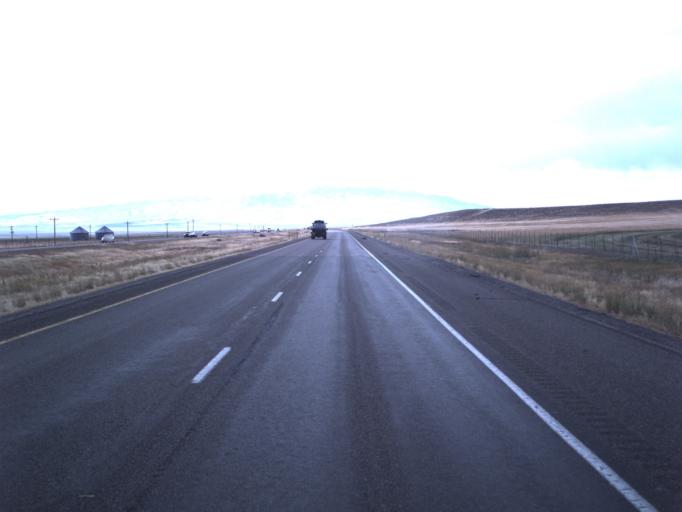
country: US
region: Idaho
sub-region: Oneida County
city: Malad City
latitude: 41.9793
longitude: -112.7979
